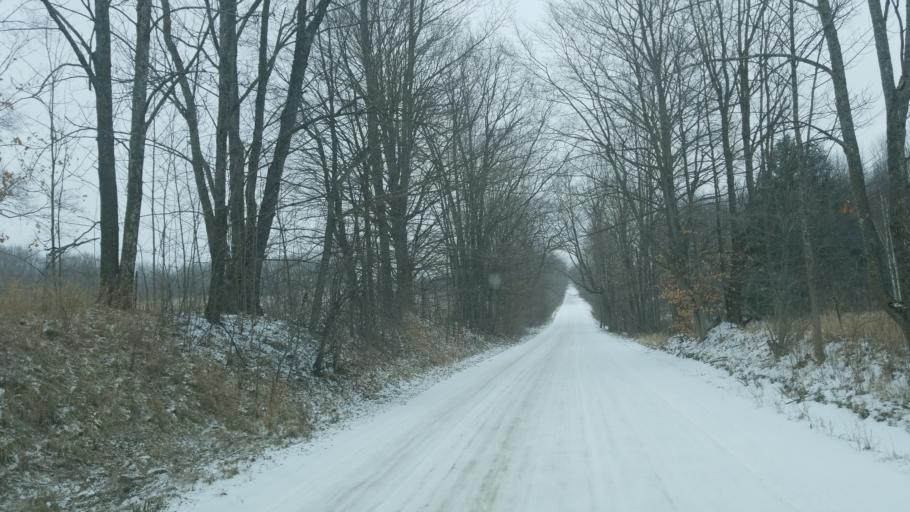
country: US
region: Michigan
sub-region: Osceola County
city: Evart
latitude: 44.0160
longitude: -85.2400
